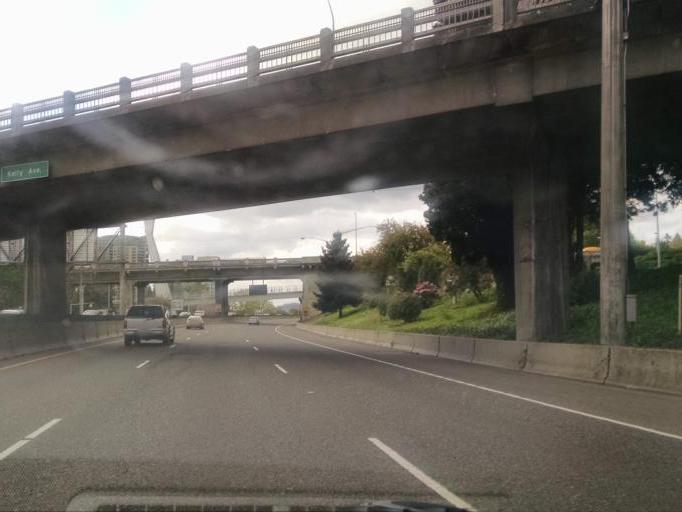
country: US
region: Oregon
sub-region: Multnomah County
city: Portland
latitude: 45.5020
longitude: -122.6738
